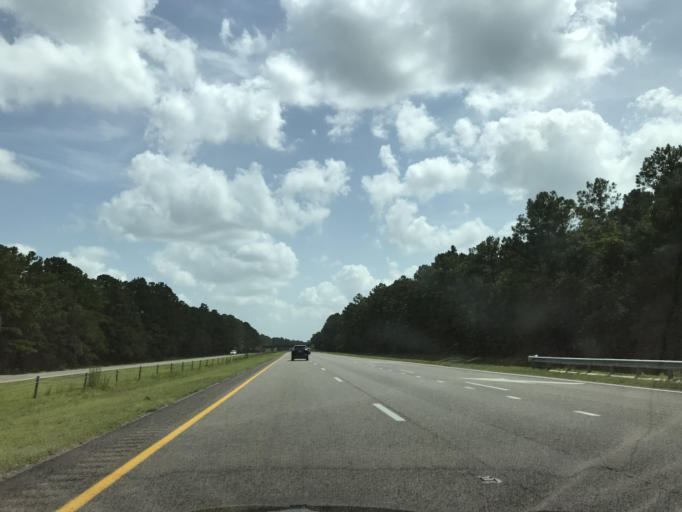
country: US
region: North Carolina
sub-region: Pender County
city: Burgaw
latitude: 34.5720
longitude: -77.9004
